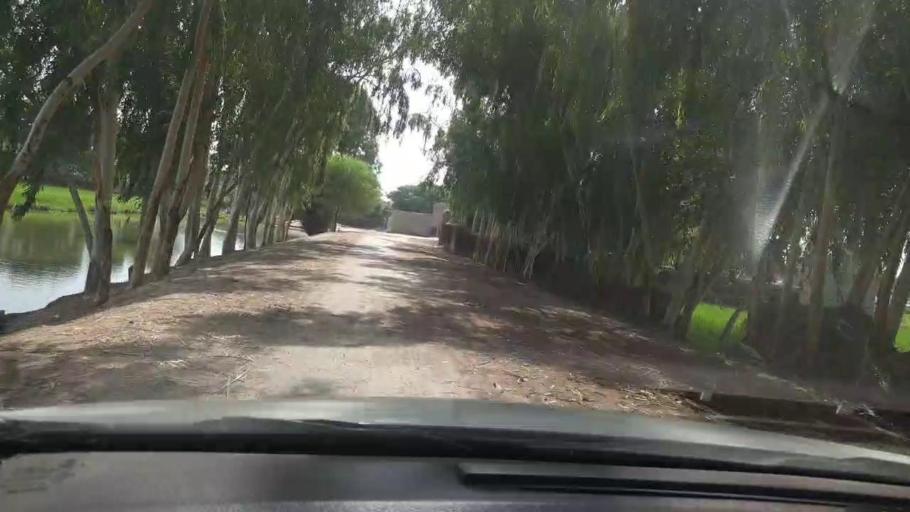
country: PK
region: Sindh
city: Rustam jo Goth
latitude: 27.9734
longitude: 68.7775
